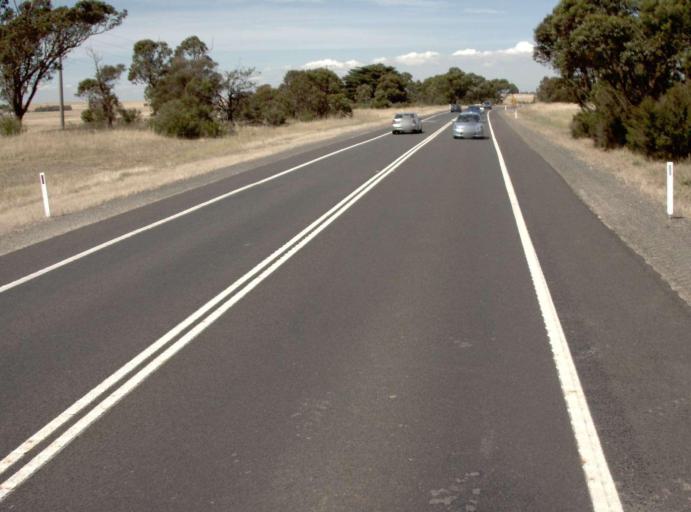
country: AU
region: Victoria
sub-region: Wellington
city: Heyfield
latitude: -38.1323
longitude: 146.8121
